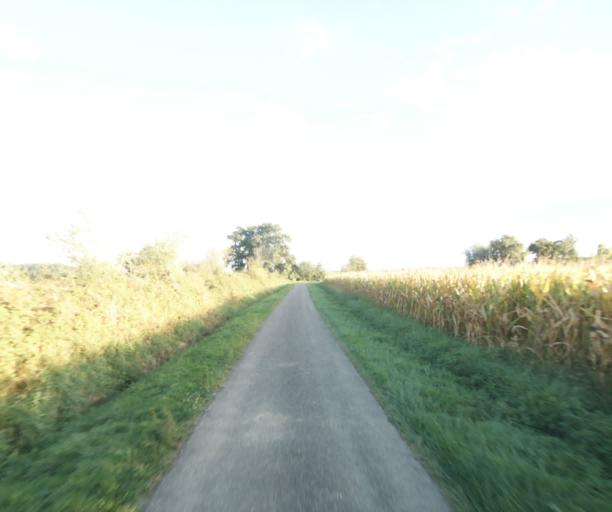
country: FR
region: Midi-Pyrenees
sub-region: Departement du Gers
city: Le Houga
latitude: 43.8275
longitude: -0.1116
